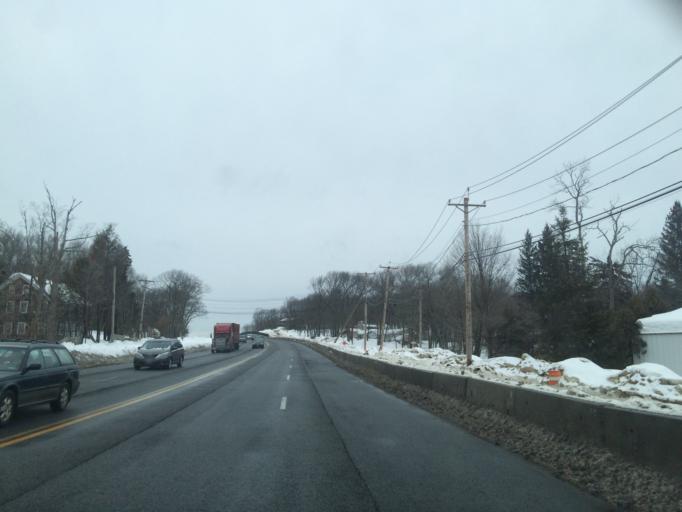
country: US
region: Massachusetts
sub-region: Middlesex County
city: Lincoln
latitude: 42.4455
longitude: -71.3084
